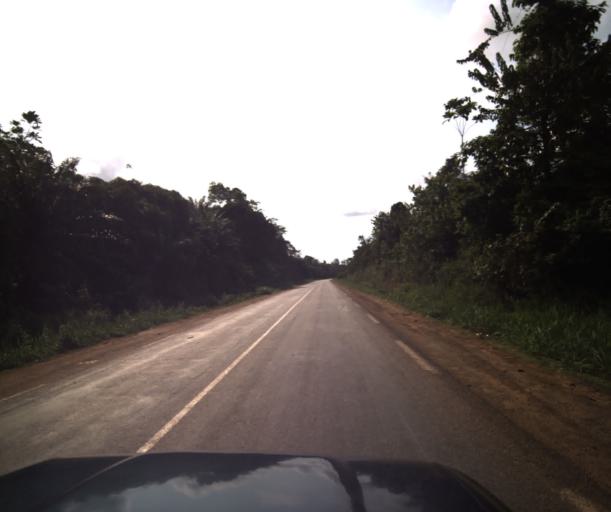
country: CM
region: Littoral
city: Edea
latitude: 3.9459
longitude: 10.0424
